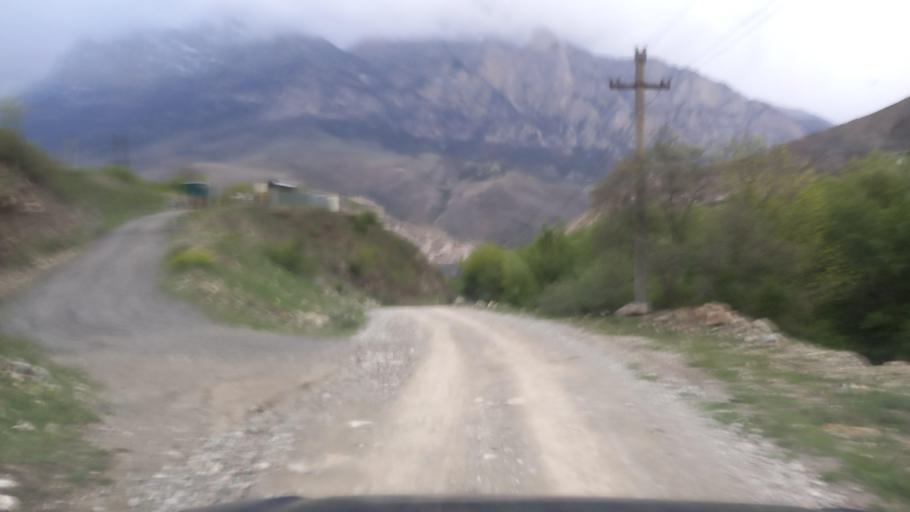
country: RU
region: North Ossetia
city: Mizur
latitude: 42.8503
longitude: 44.1556
